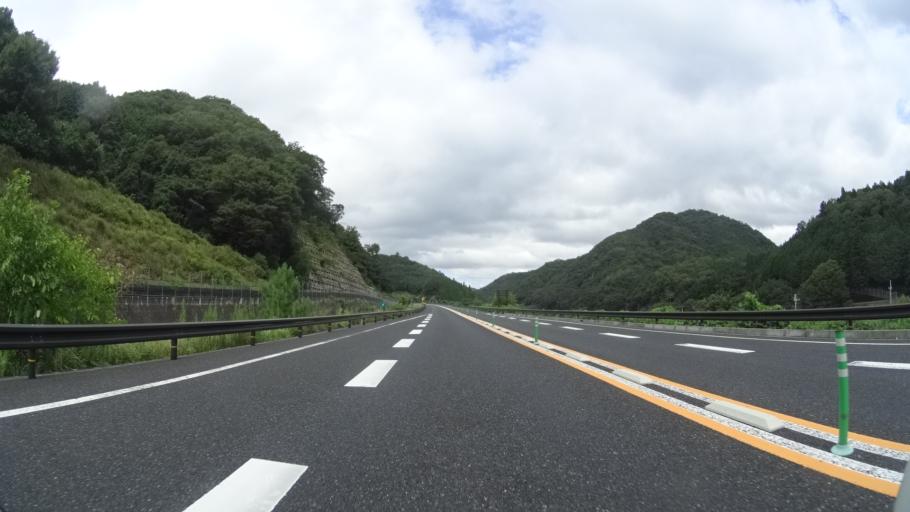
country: JP
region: Hyogo
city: Yamazakicho-nakabirose
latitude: 35.0591
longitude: 134.3650
